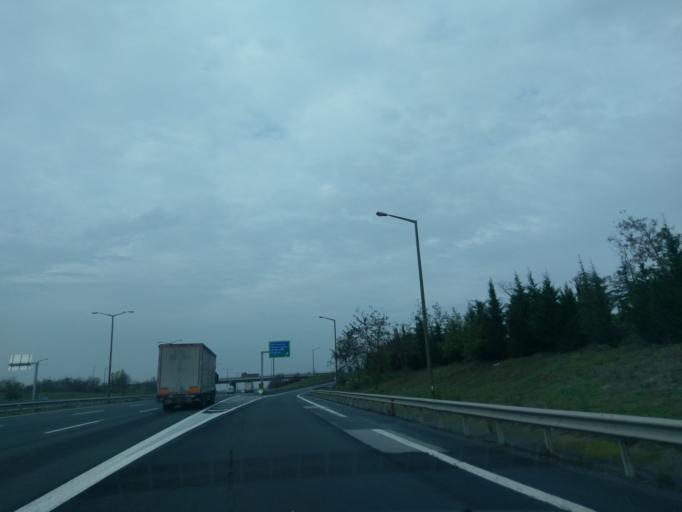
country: TR
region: Istanbul
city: Buyukcavuslu
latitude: 41.1921
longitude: 28.0877
